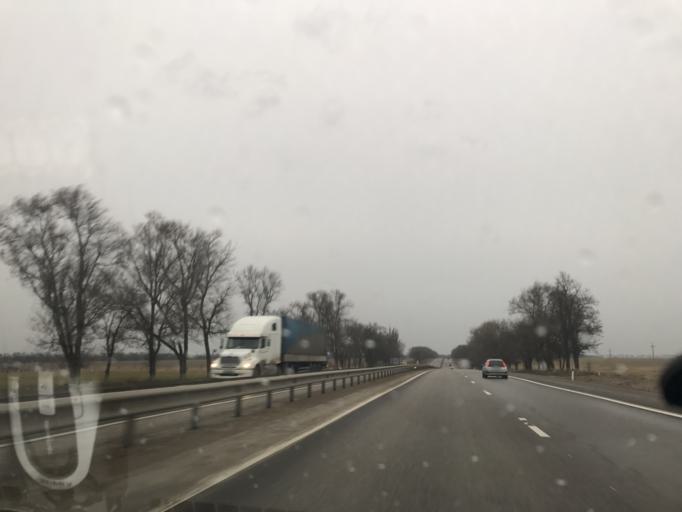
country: RU
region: Krasnodarskiy
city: Pavlovskaya
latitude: 46.1643
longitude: 39.8425
